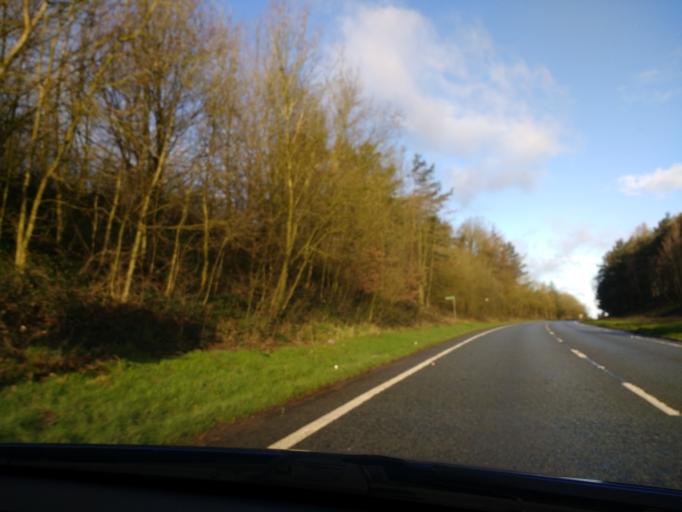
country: GB
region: England
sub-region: Cumbria
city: Cockermouth
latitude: 54.6543
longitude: -3.3753
